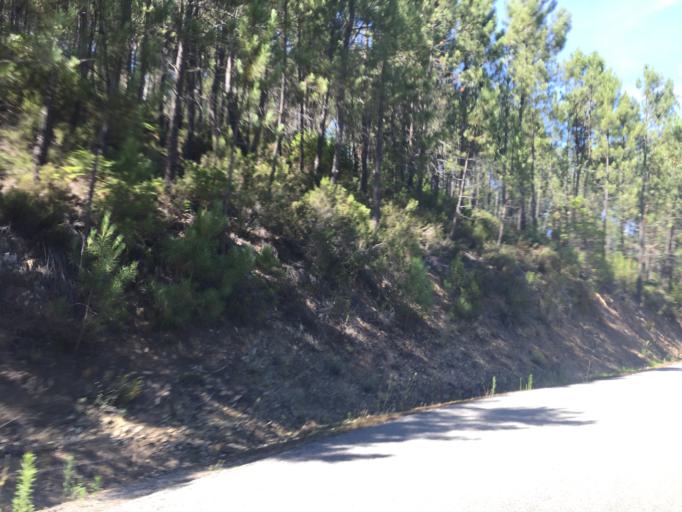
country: PT
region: Castelo Branco
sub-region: Oleiros
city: Oleiros
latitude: 39.9823
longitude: -7.8489
